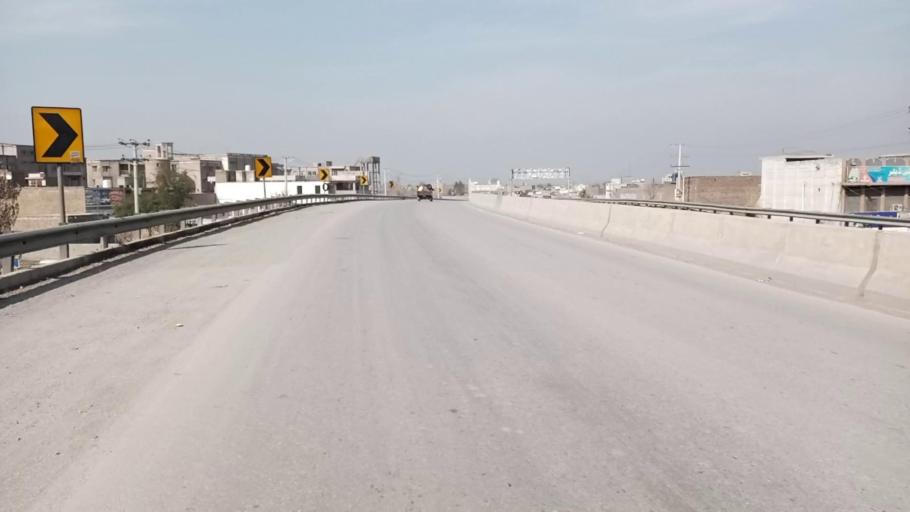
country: PK
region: Khyber Pakhtunkhwa
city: Peshawar
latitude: 34.0297
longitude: 71.6424
